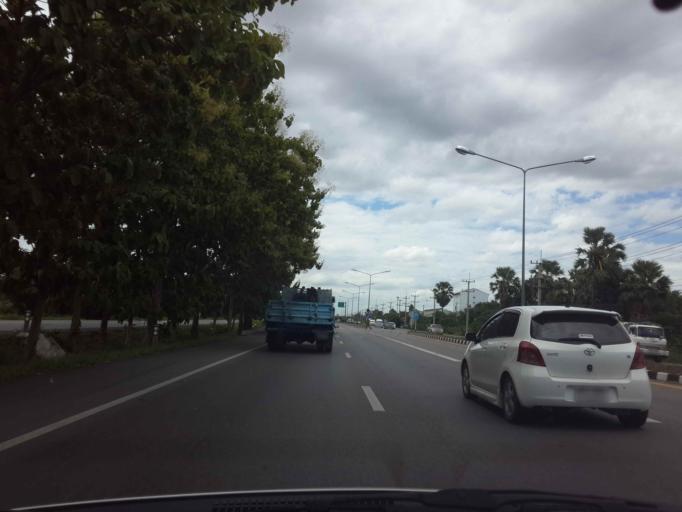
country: TH
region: Phetchaburi
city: Khao Yoi
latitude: 13.1534
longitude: 99.8502
